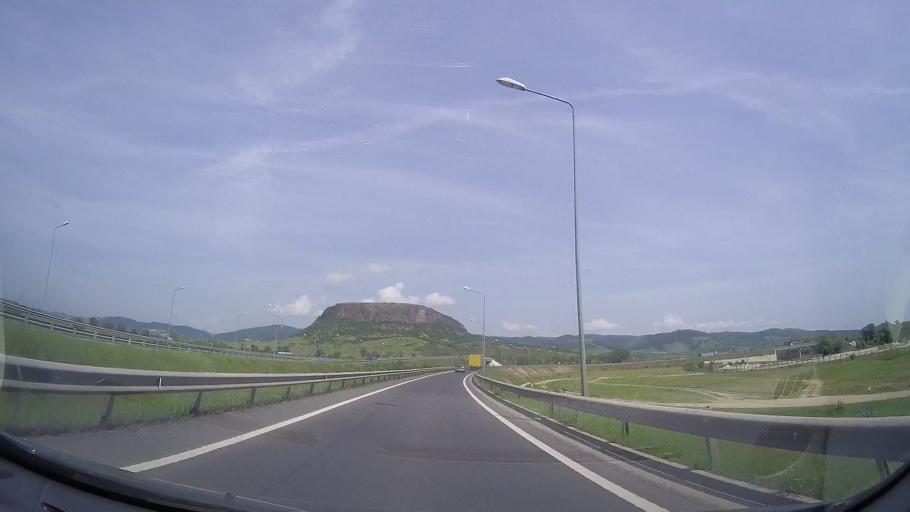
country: RO
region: Hunedoara
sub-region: Oras Simeria
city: Simeria
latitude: 45.8456
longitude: 23.0443
